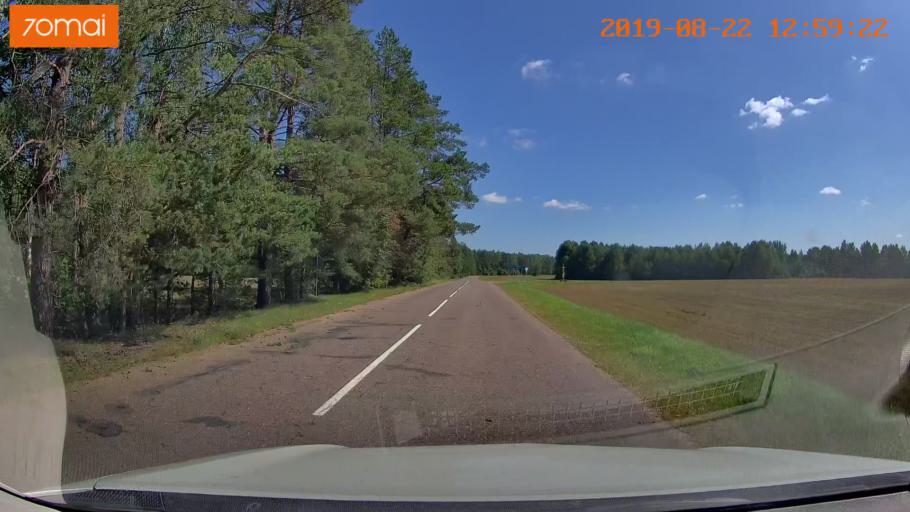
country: BY
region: Minsk
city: Prawdzinski
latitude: 53.4228
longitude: 27.7890
